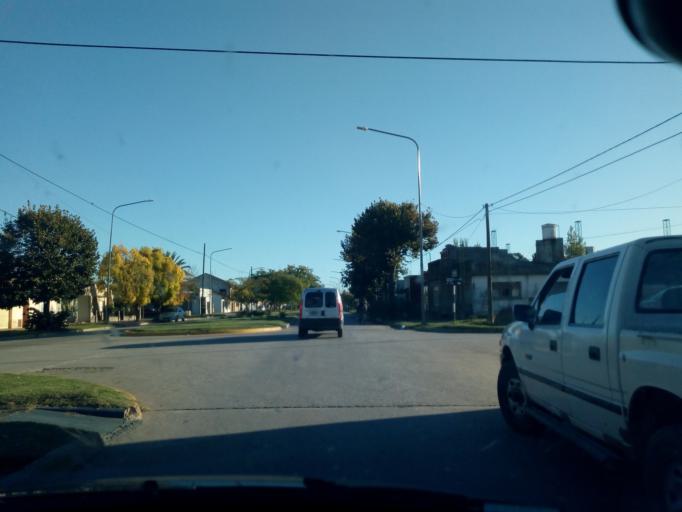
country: AR
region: Buenos Aires
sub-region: Partido de Loberia
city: Loberia
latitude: -38.1572
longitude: -58.7754
